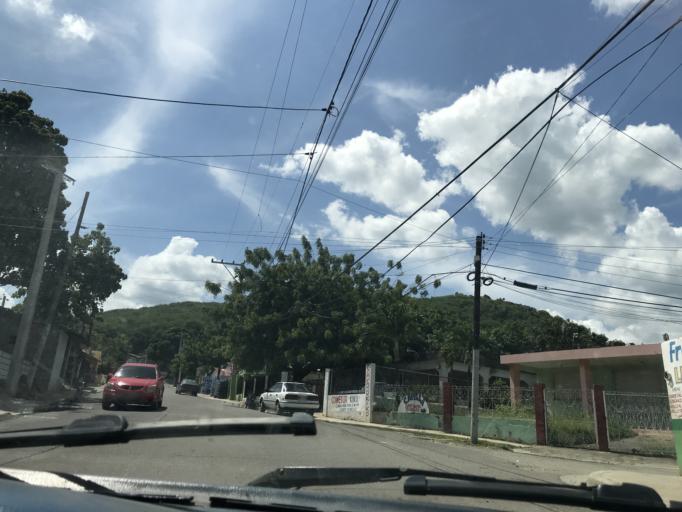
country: DO
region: Santiago
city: Tamboril
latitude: 19.5029
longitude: -70.6514
